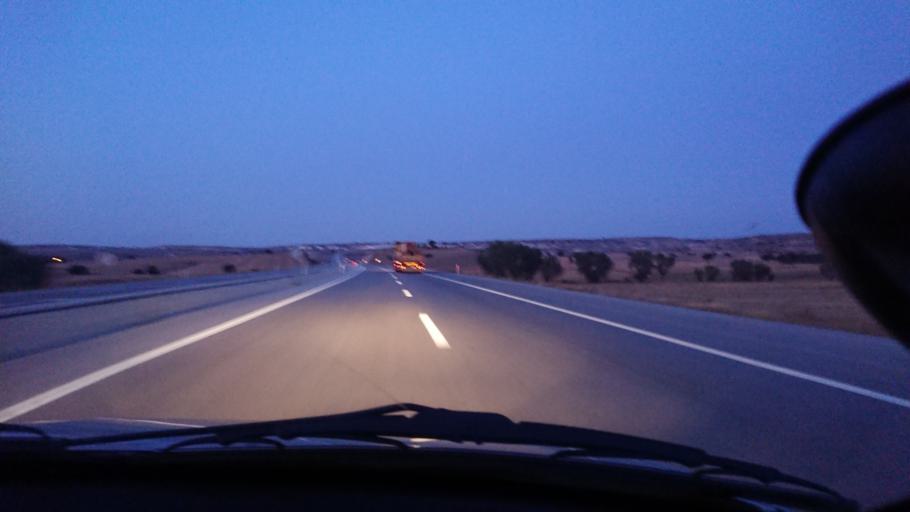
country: TR
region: Kuetahya
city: Cavdarhisar
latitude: 39.1282
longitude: 29.5458
